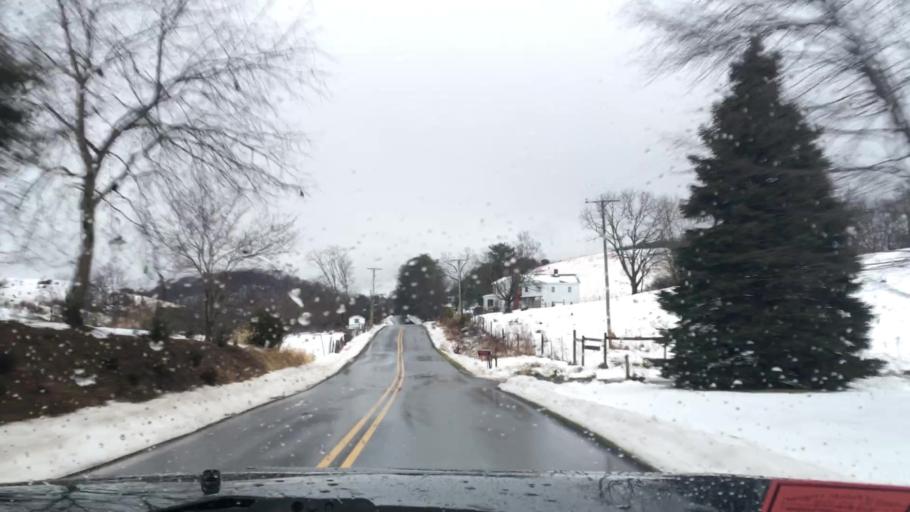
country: US
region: Virginia
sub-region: Pulaski County
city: Dublin
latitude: 37.0174
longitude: -80.6386
